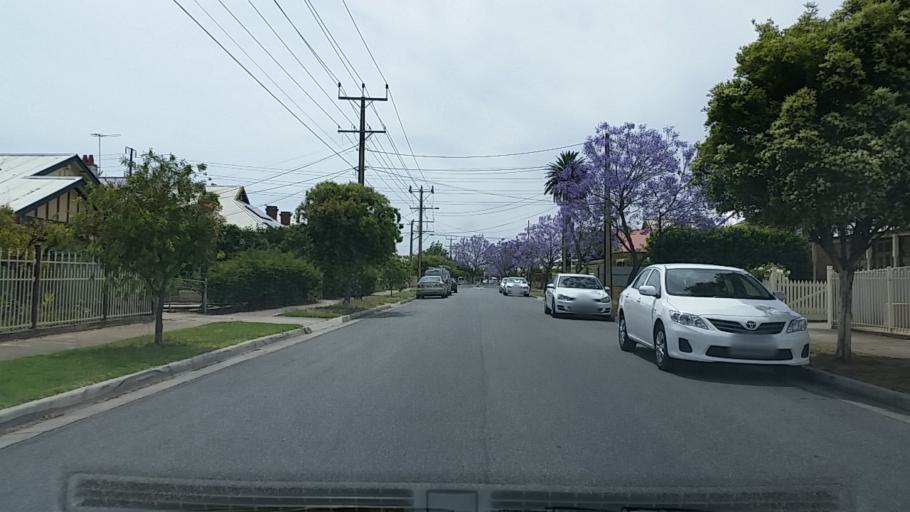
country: AU
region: South Australia
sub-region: Charles Sturt
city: Allenby Gardens
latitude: -34.8932
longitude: 138.5625
